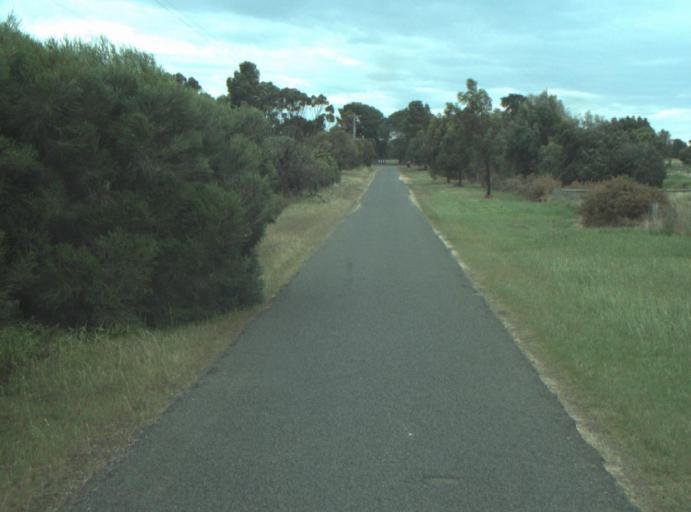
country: AU
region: Victoria
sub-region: Greater Geelong
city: Leopold
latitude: -38.2155
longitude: 144.4497
